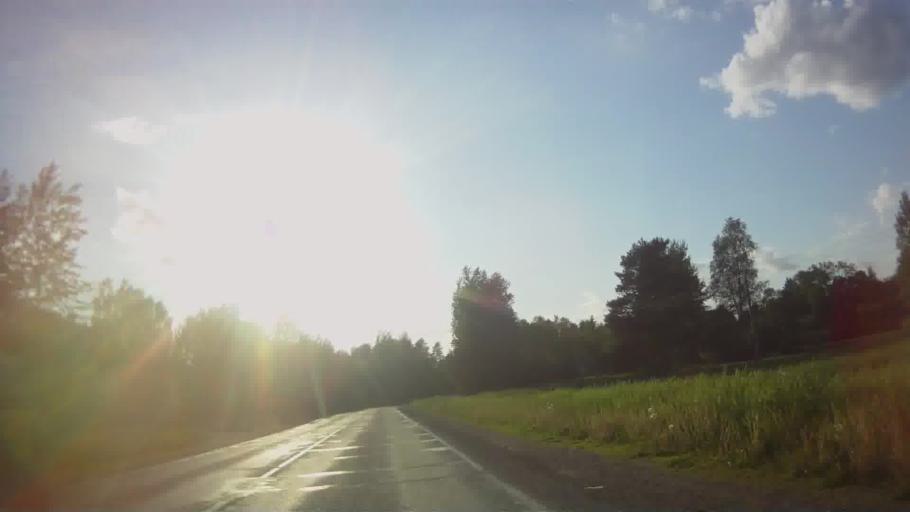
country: LV
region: Rezekne
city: Rezekne
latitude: 56.5328
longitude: 27.3100
